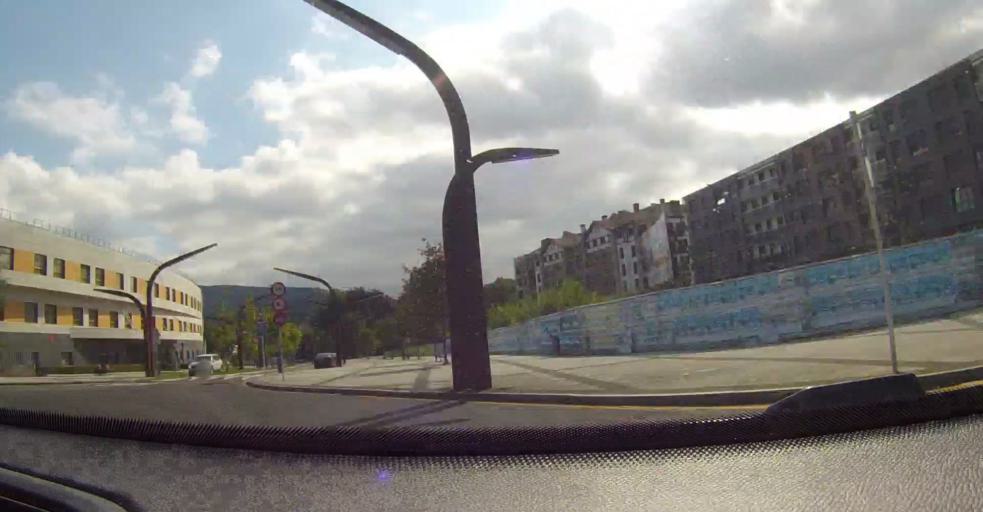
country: ES
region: Basque Country
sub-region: Bizkaia
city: Amorebieta
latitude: 43.2213
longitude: -2.7288
